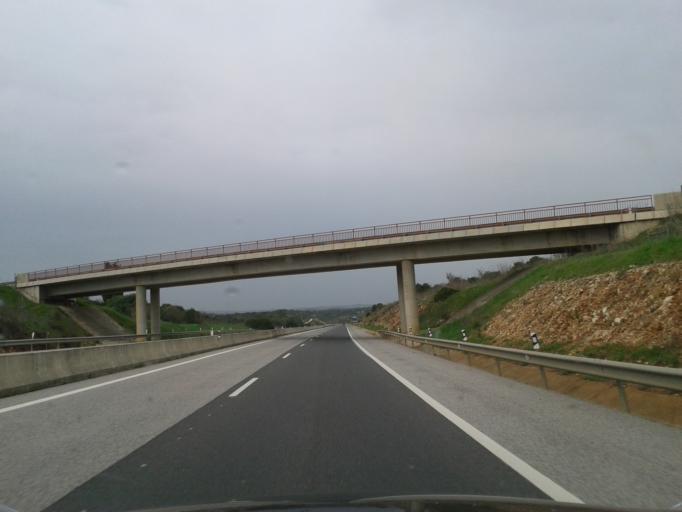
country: PT
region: Faro
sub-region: Lagos
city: Lagos
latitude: 37.1226
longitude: -8.7077
